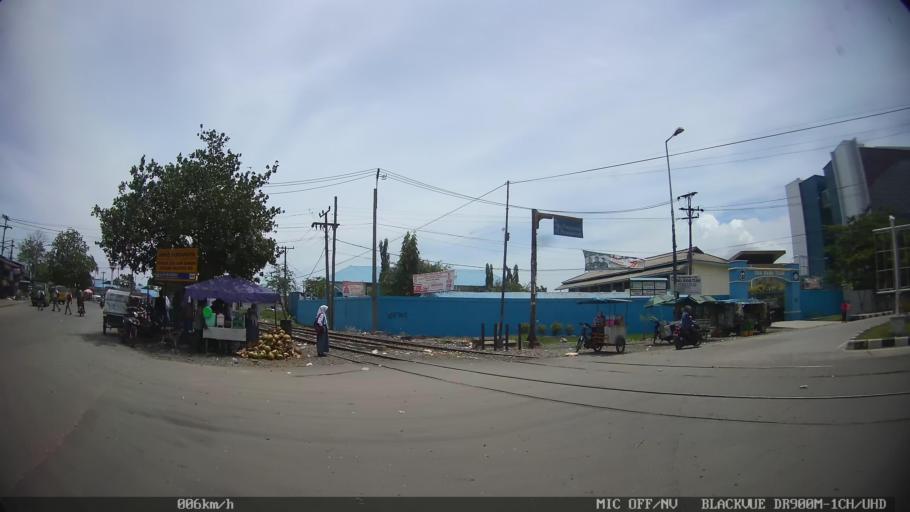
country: ID
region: North Sumatra
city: Belawan
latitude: 3.7828
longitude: 98.6882
